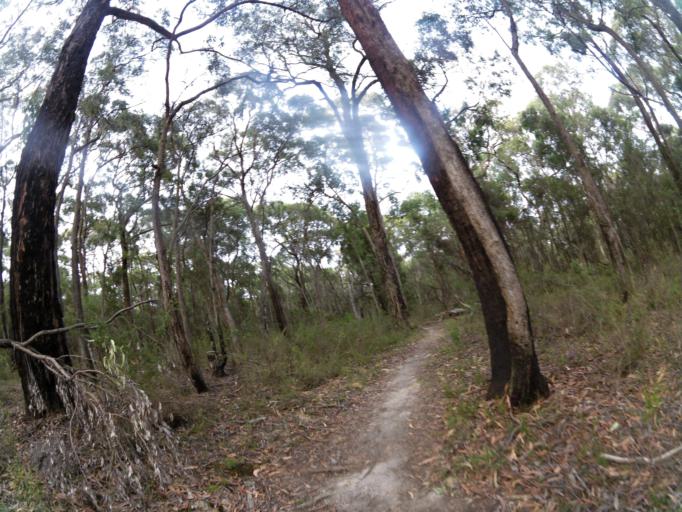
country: AU
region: Victoria
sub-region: Colac-Otway
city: Colac
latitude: -38.4905
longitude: 143.6995
